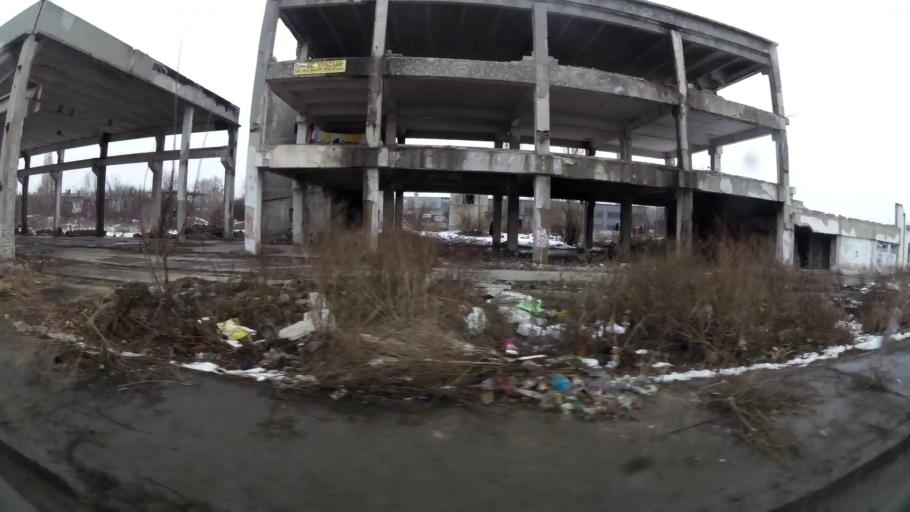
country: RO
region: Ilfov
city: Dobroesti
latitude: 44.4217
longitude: 26.1866
